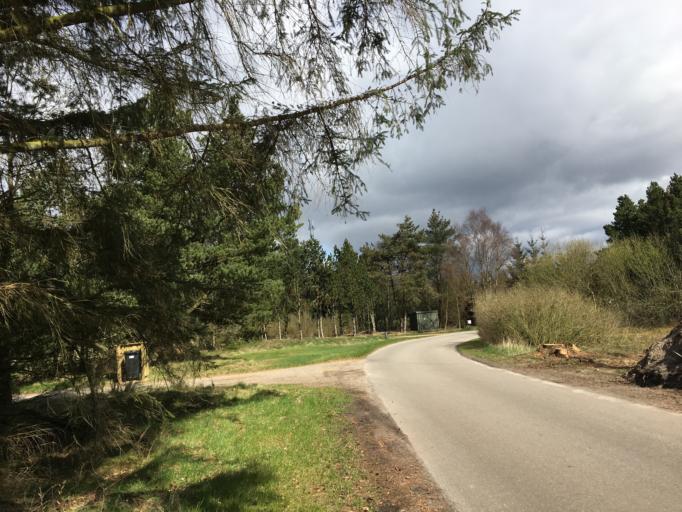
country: DK
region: South Denmark
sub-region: Varde Kommune
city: Oksbol
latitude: 55.5613
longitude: 8.2189
